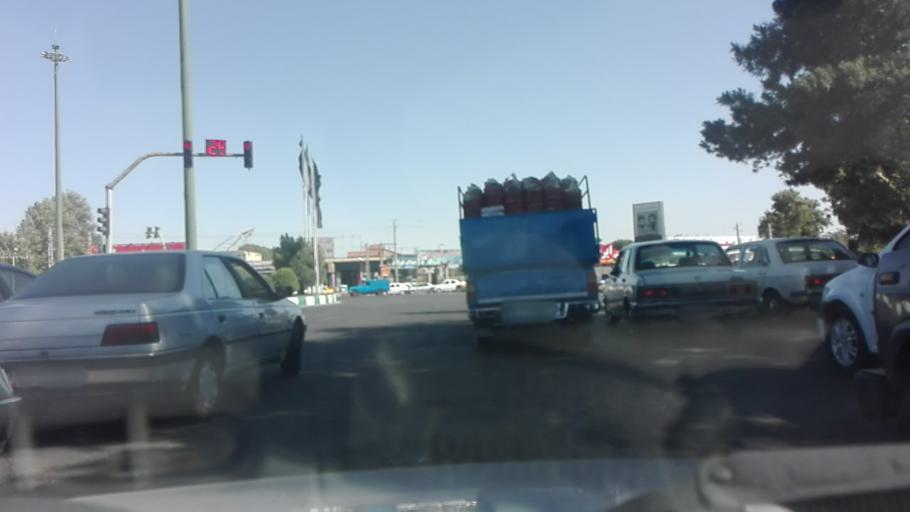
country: IR
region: Tehran
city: Shahriar
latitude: 35.6520
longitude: 51.0511
